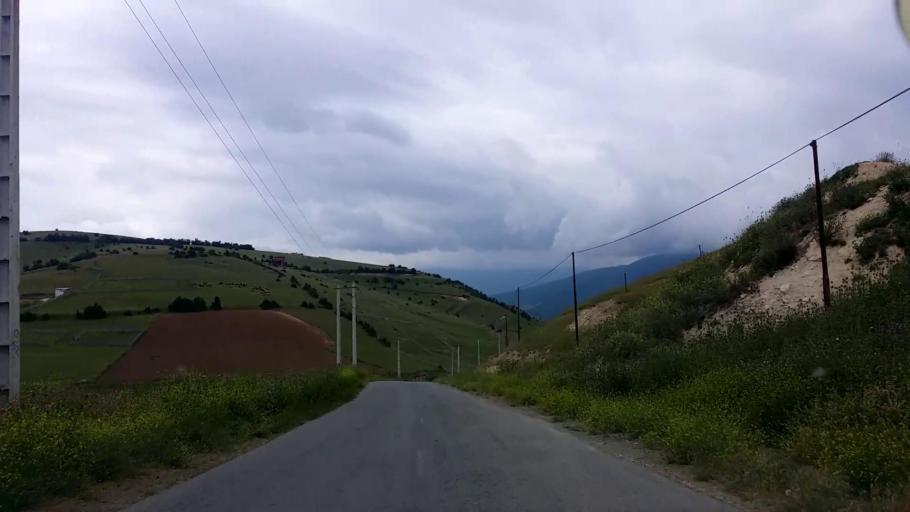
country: IR
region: Mazandaran
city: Chalus
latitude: 36.5284
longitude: 51.2683
